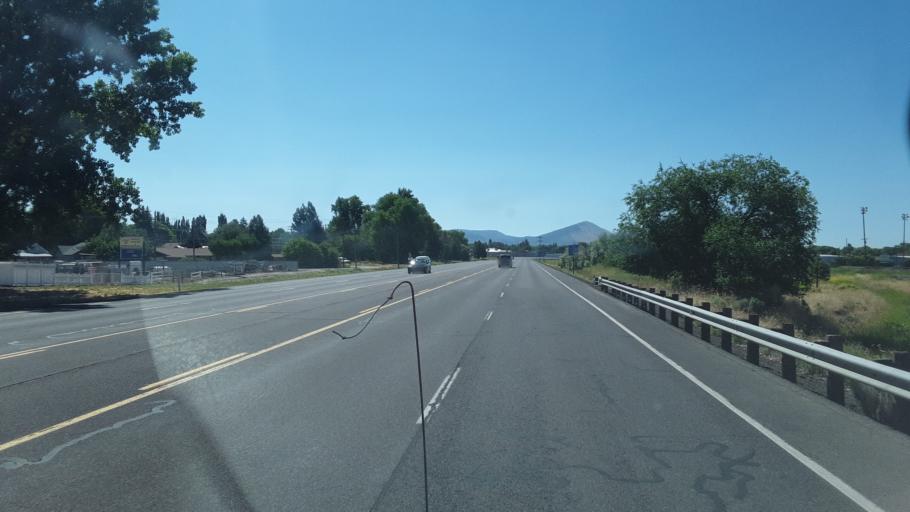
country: US
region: Oregon
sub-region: Klamath County
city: Altamont
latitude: 42.2122
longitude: -121.7417
